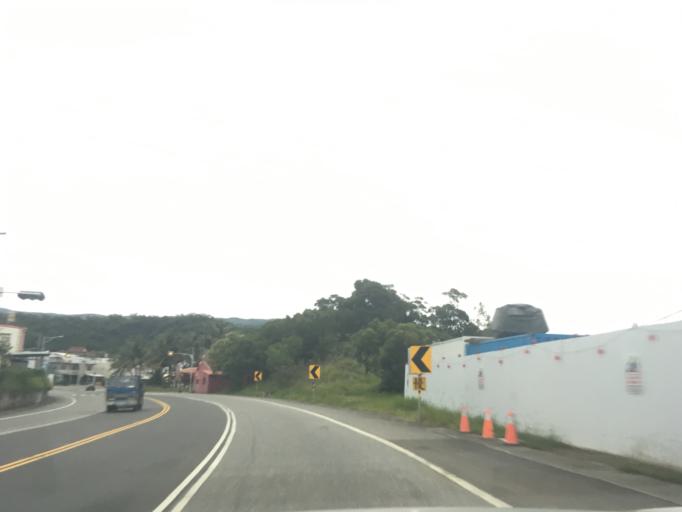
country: TW
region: Taiwan
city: Hengchun
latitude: 22.3370
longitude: 120.8942
